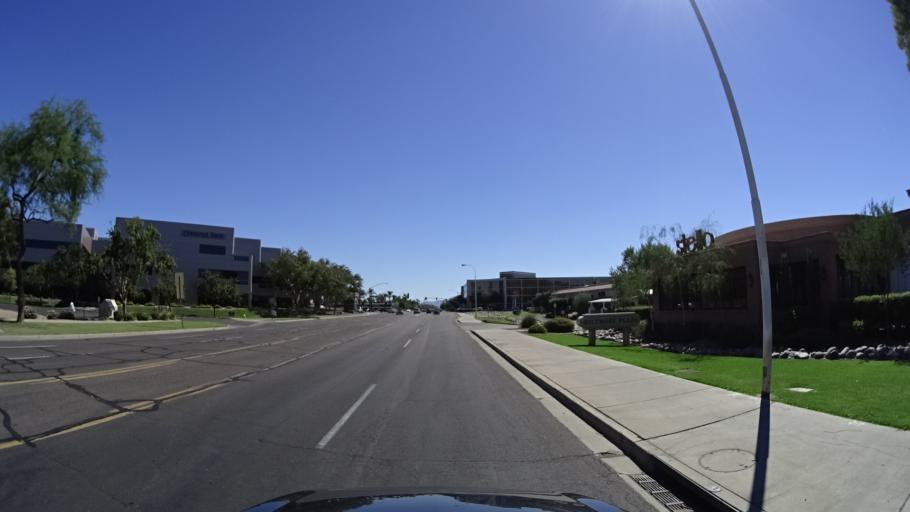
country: US
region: Arizona
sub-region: Maricopa County
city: Paradise Valley
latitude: 33.5116
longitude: -112.0131
